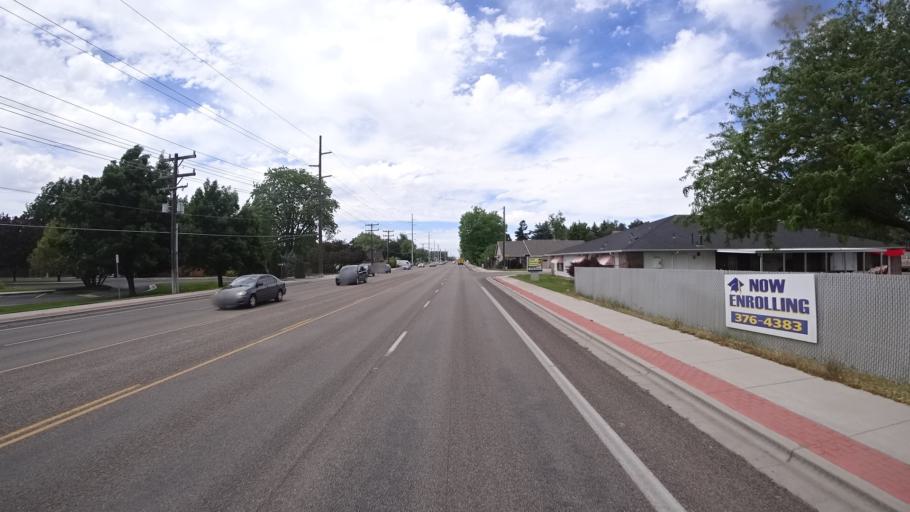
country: US
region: Idaho
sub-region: Ada County
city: Garden City
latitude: 43.6338
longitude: -116.2888
